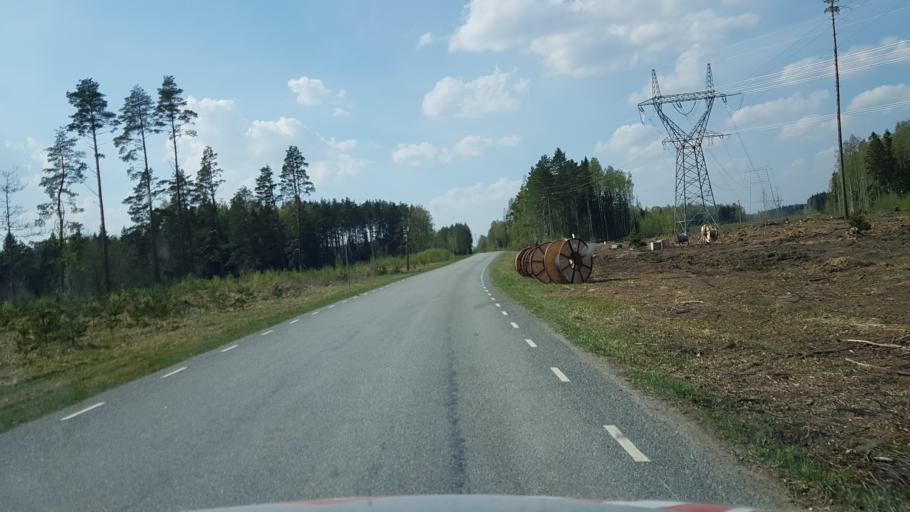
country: EE
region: Paernumaa
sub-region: Paikuse vald
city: Paikuse
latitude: 58.4420
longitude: 24.6030
